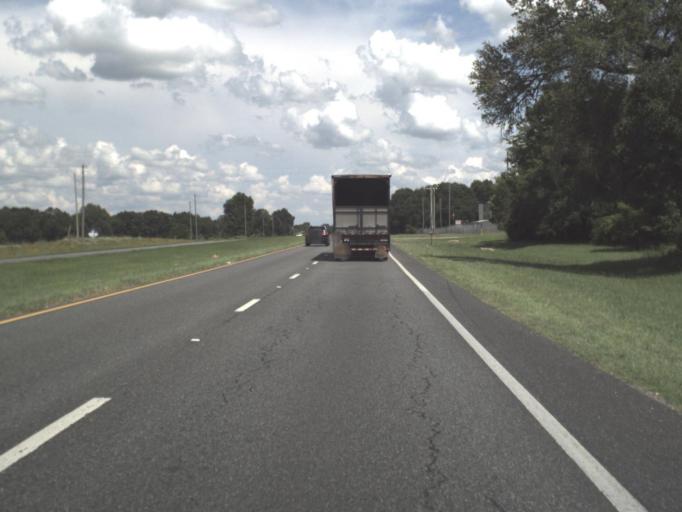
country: US
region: Florida
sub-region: Alachua County
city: High Springs
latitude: 29.8152
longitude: -82.5701
